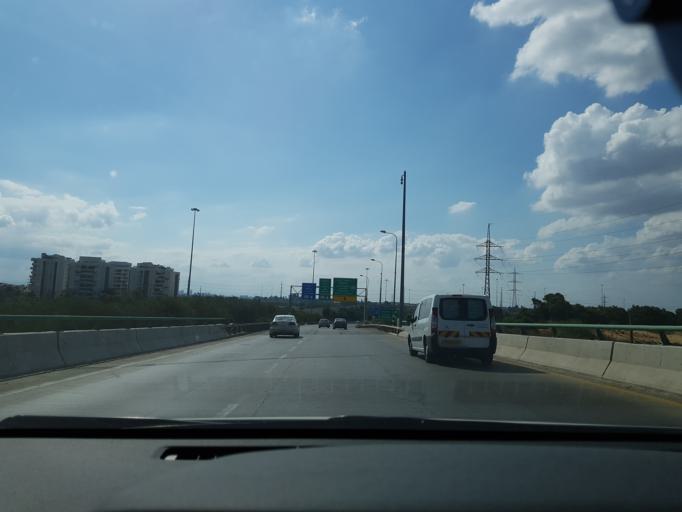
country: IL
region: Central District
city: Rishon LeZiyyon
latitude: 31.9622
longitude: 34.7848
